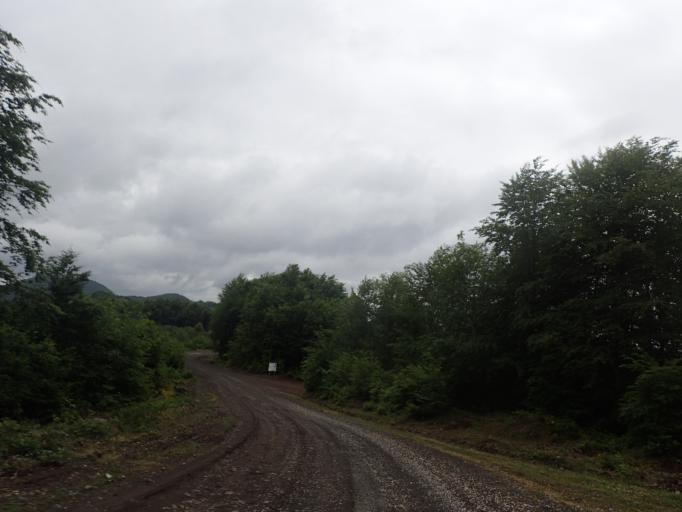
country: TR
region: Samsun
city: Salipazari
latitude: 40.9123
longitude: 36.8681
